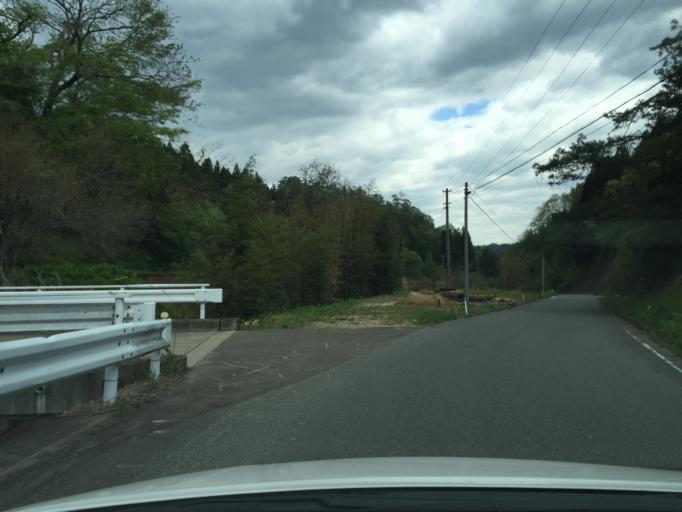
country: JP
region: Fukushima
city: Hobaramachi
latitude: 37.7158
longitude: 140.6422
